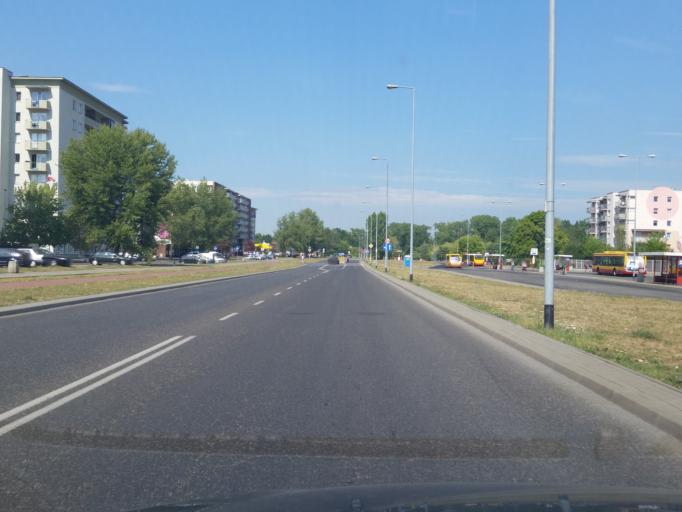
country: PL
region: Masovian Voivodeship
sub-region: Warszawa
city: Bialoleka
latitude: 52.3332
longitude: 20.9416
